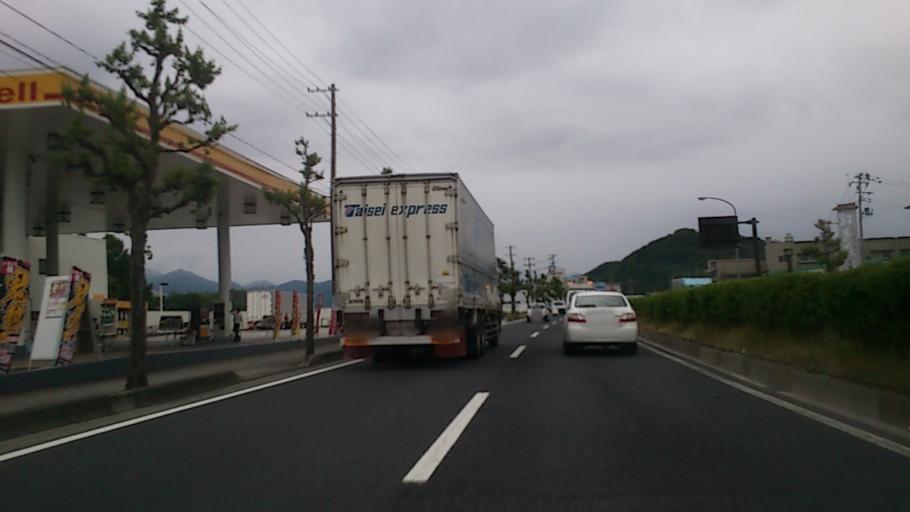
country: JP
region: Yamagata
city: Tendo
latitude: 38.3587
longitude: 140.3888
